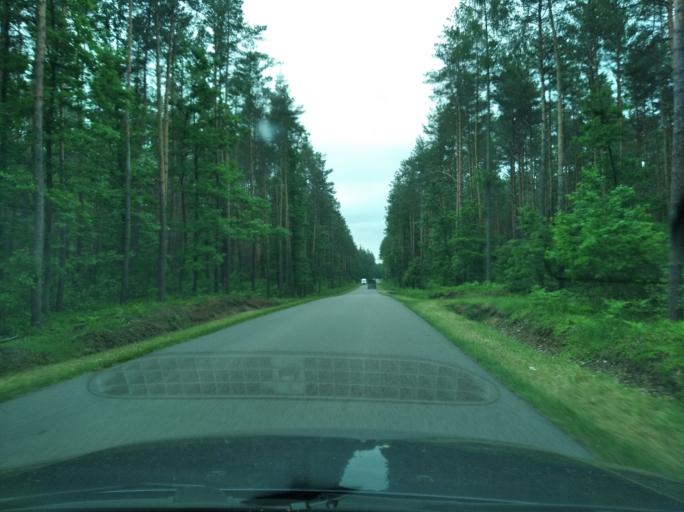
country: PL
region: Subcarpathian Voivodeship
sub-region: Powiat kolbuszowski
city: Niwiska
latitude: 50.1936
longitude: 21.6562
